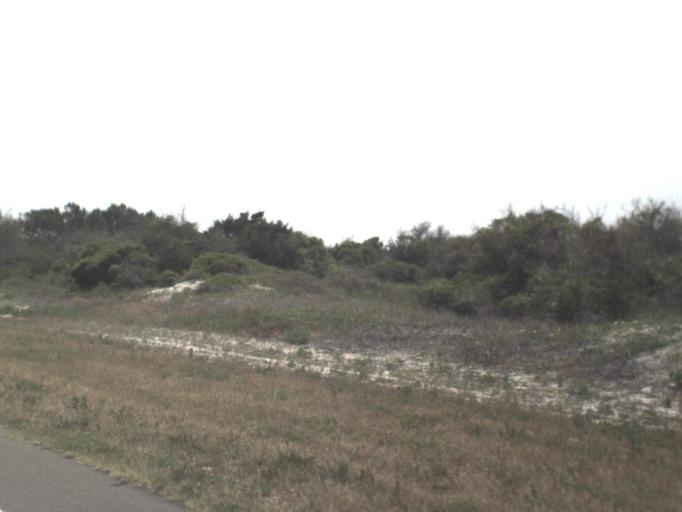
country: US
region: Florida
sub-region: Duval County
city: Atlantic Beach
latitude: 30.4350
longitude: -81.4139
